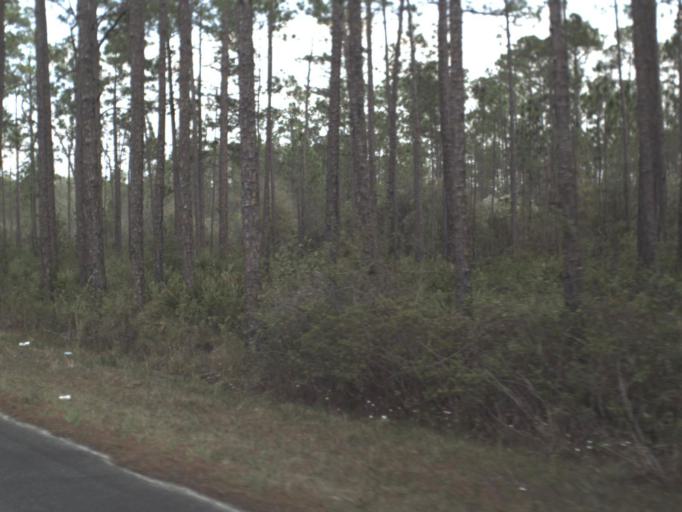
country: US
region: Florida
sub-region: Franklin County
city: Apalachicola
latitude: 29.9672
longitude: -84.9756
